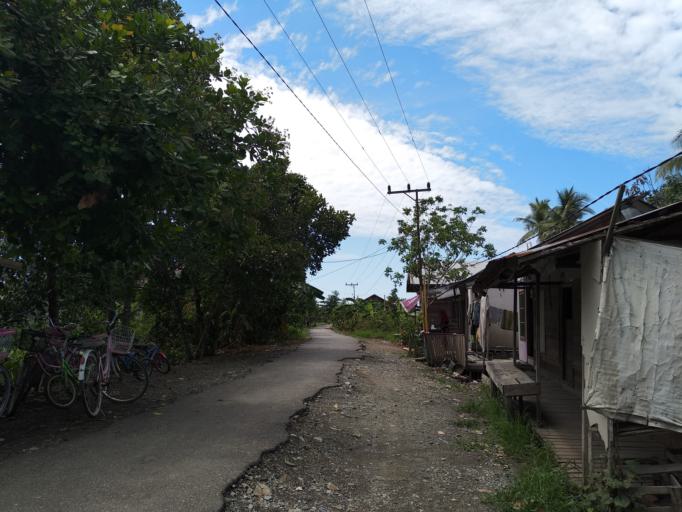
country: ID
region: South Kalimantan
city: Tabunganen
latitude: -3.4139
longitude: 114.4907
